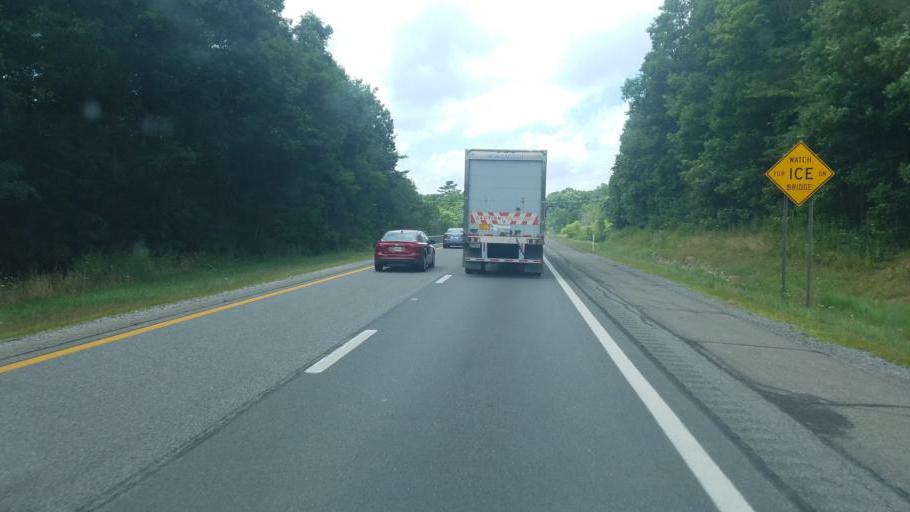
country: US
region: West Virginia
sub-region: Raleigh County
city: Shady Spring
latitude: 37.6803
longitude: -81.1222
